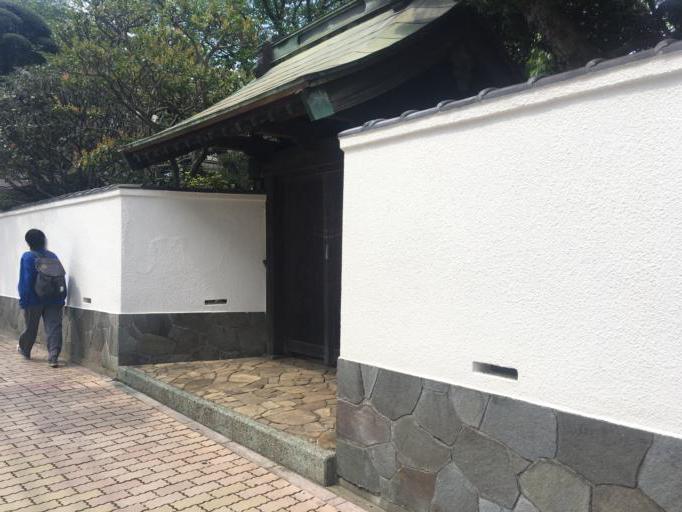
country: JP
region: Saitama
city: Wako
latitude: 35.7864
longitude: 139.6098
